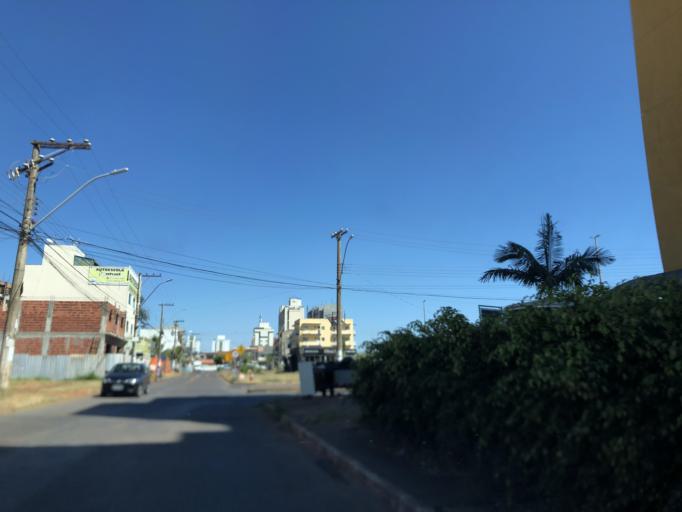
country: BR
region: Federal District
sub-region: Brasilia
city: Brasilia
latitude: -15.8655
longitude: -48.0585
